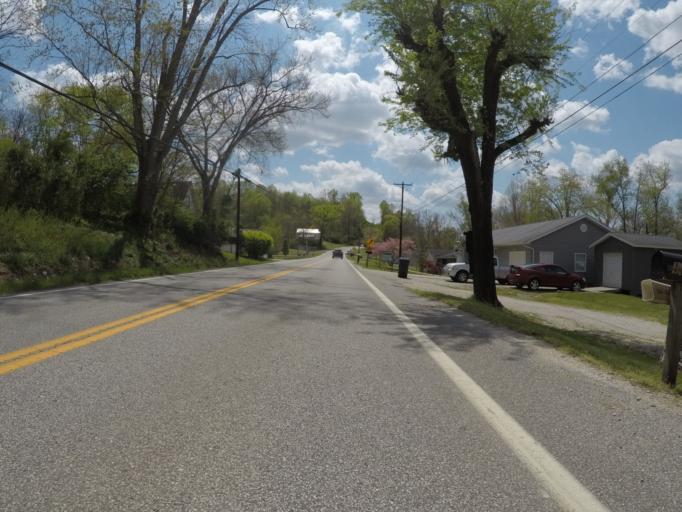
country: US
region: West Virginia
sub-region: Cabell County
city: Pea Ridge
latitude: 38.4538
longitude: -82.3755
